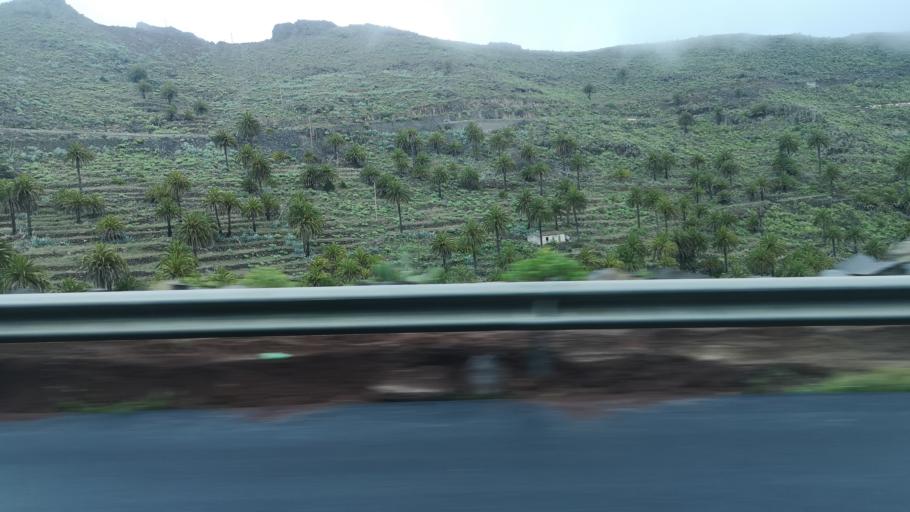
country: ES
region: Canary Islands
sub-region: Provincia de Santa Cruz de Tenerife
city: Alajero
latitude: 28.0750
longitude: -17.2077
